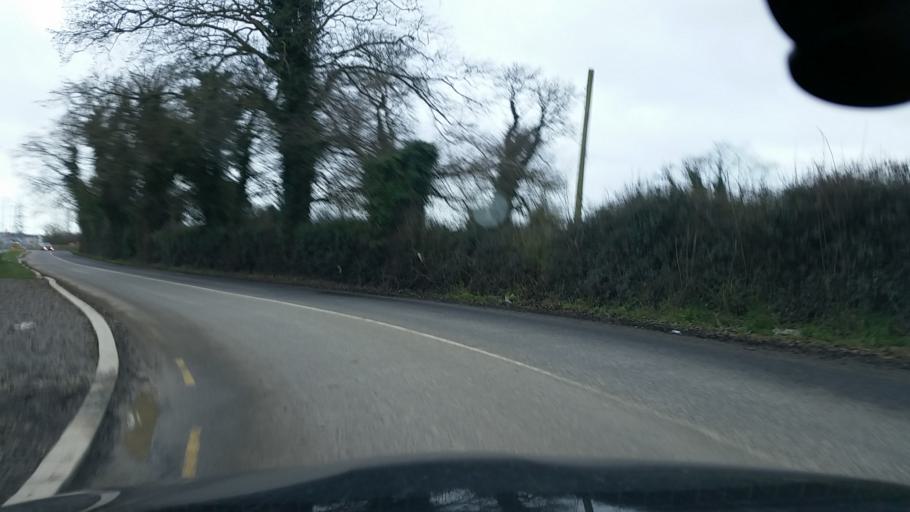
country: IE
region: Leinster
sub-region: Fingal County
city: Blanchardstown
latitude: 53.4252
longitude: -6.3773
